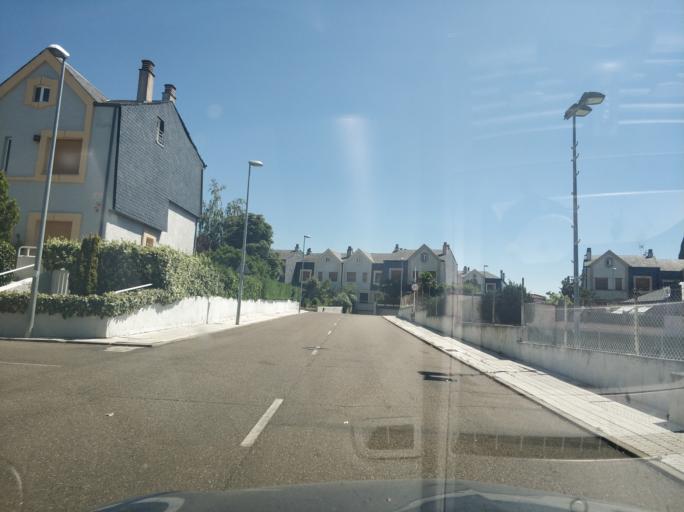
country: ES
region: Castille and Leon
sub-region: Provincia de Salamanca
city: Villares de la Reina
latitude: 40.9954
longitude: -5.6609
